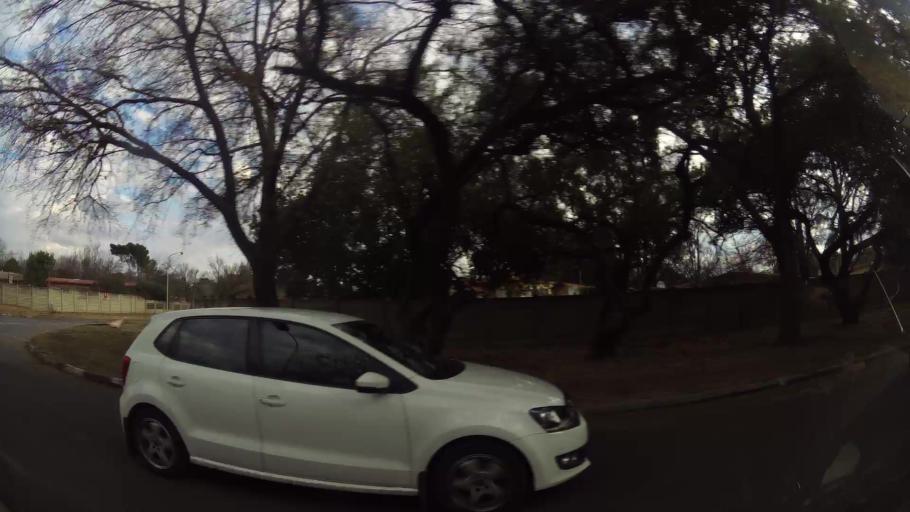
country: ZA
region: Orange Free State
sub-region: Fezile Dabi District Municipality
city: Sasolburg
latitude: -26.8060
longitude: 27.8180
